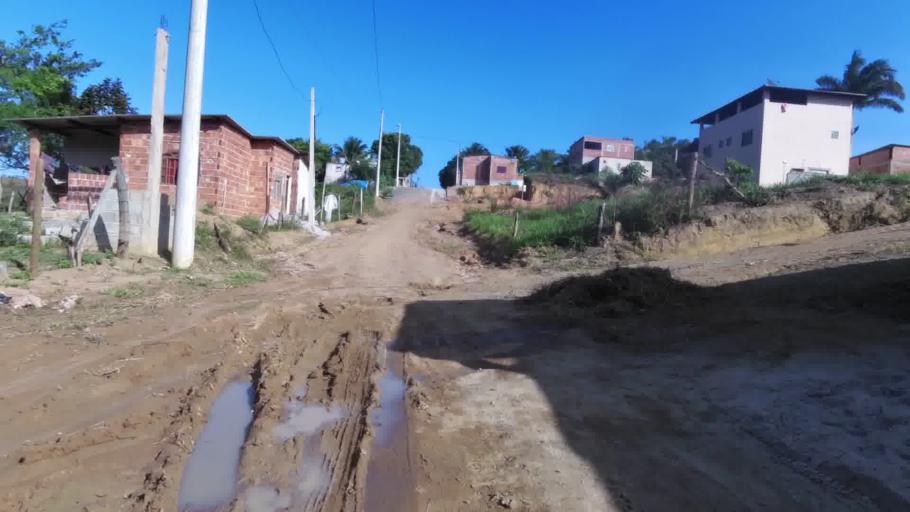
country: BR
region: Espirito Santo
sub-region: Piuma
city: Piuma
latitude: -20.8157
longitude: -40.6219
